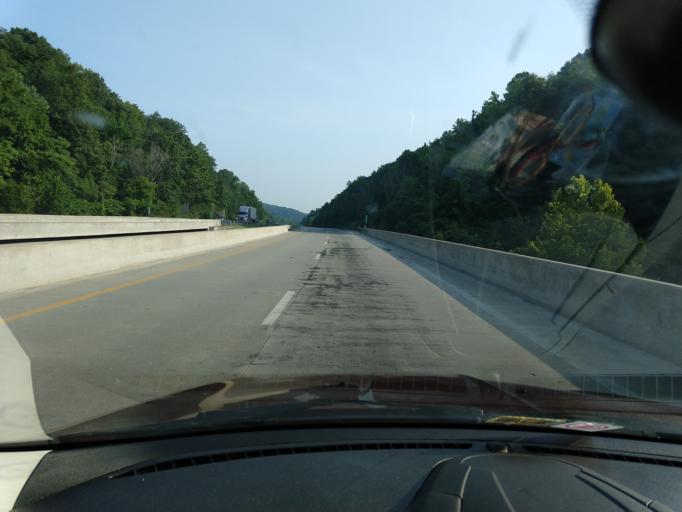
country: US
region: West Virginia
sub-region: Kanawha County
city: Sissonville
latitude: 38.4957
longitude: -81.6426
